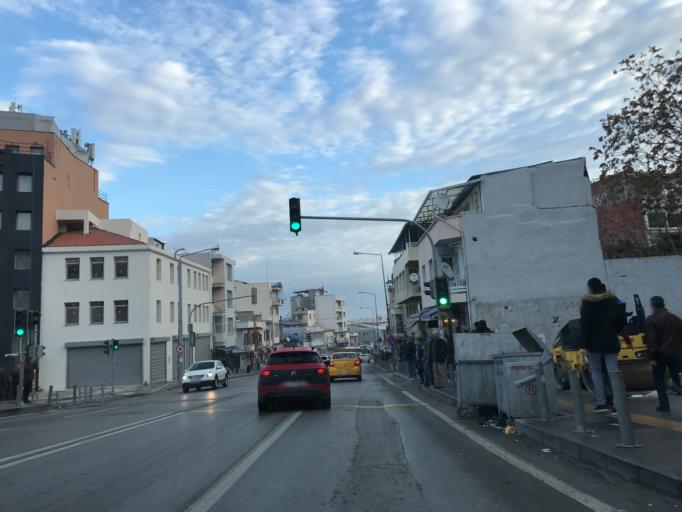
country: TR
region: Izmir
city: Izmir
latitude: 38.4158
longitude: 27.1351
